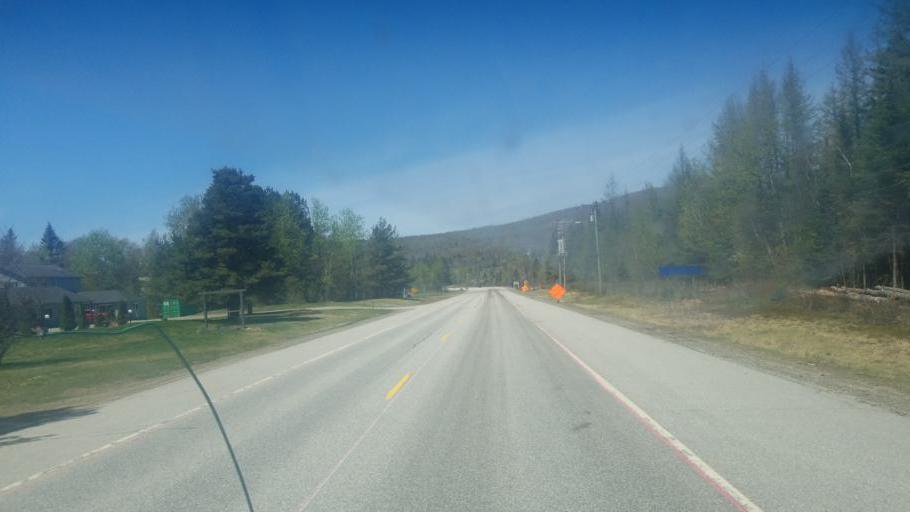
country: US
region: New Hampshire
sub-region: Coos County
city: Jefferson
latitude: 44.2673
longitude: -71.4661
